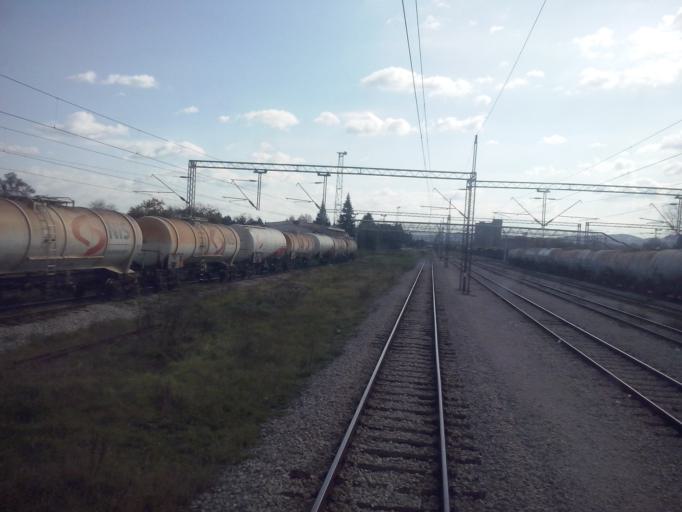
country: RS
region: Central Serbia
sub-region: Zlatiborski Okrug
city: Pozega
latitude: 43.8448
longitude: 20.0236
